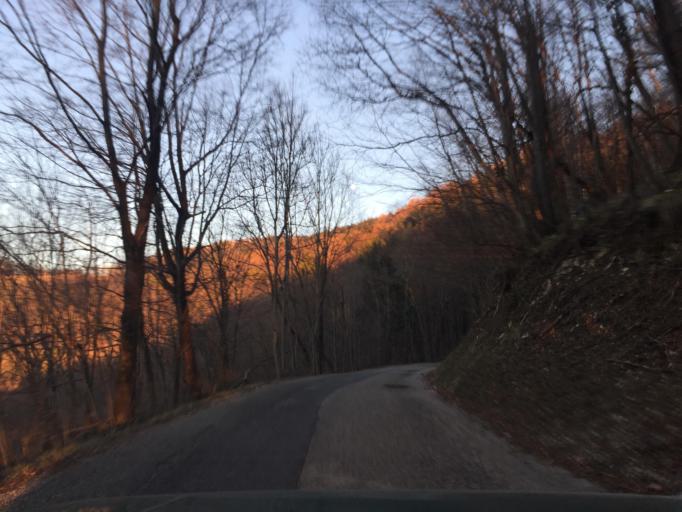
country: SI
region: Kanal
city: Kanal
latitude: 46.0708
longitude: 13.6471
